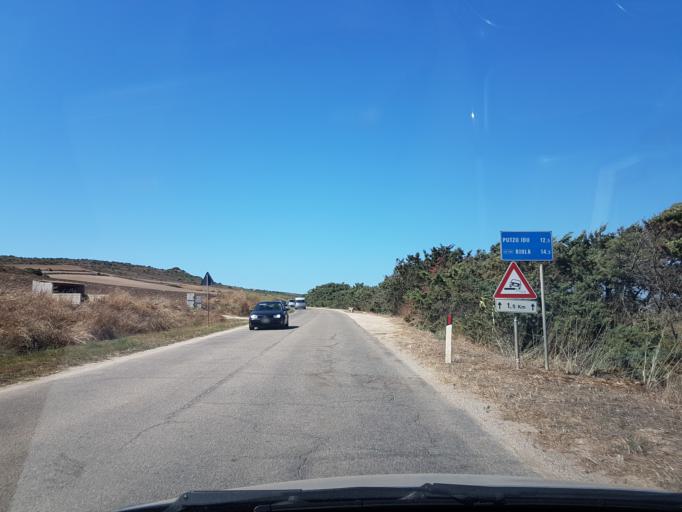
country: IT
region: Sardinia
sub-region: Provincia di Oristano
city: Cabras
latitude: 39.9329
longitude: 8.4572
